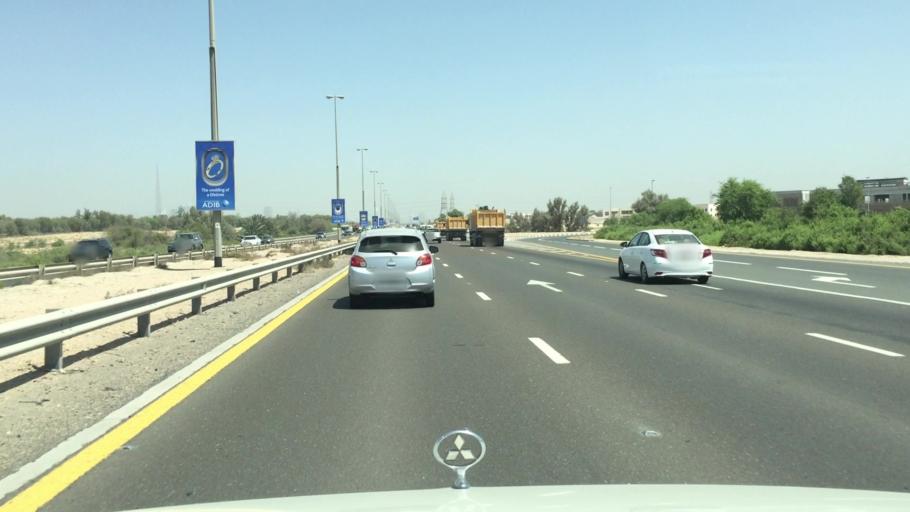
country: AE
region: Dubai
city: Dubai
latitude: 25.1406
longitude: 55.3475
